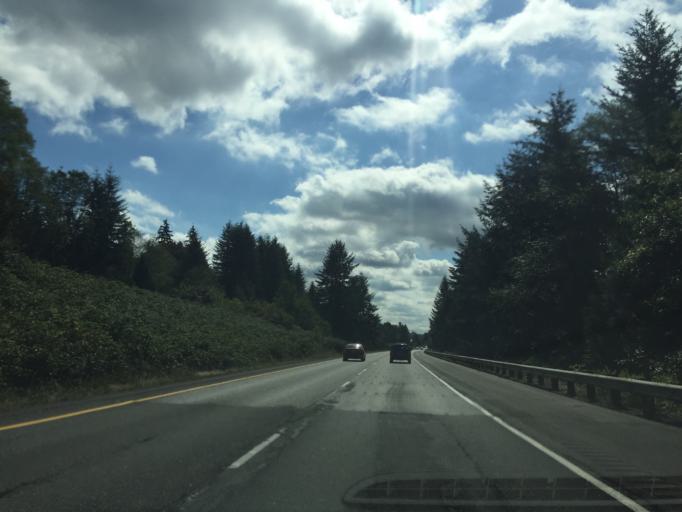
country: US
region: Washington
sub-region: Whatcom County
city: Sudden Valley
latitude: 48.6569
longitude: -122.3694
